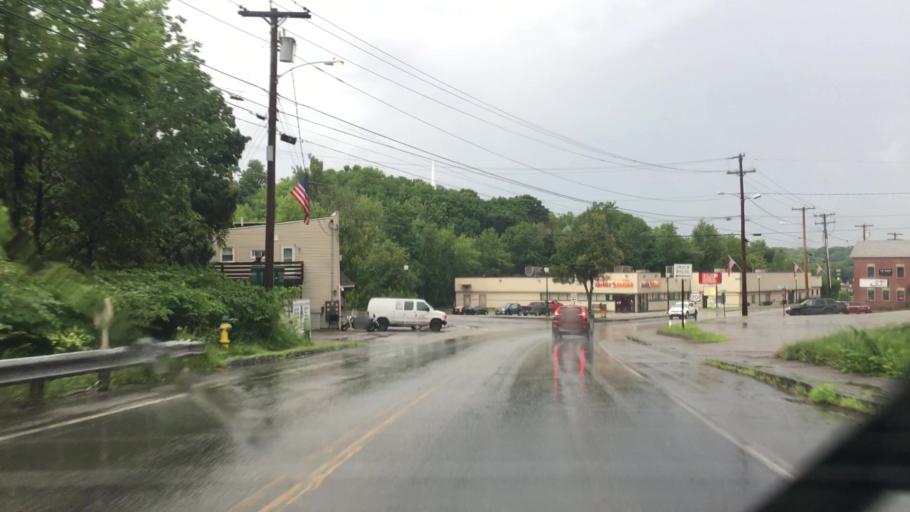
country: US
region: Maine
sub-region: Kennebec County
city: Gardiner
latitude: 44.2289
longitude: -69.7774
